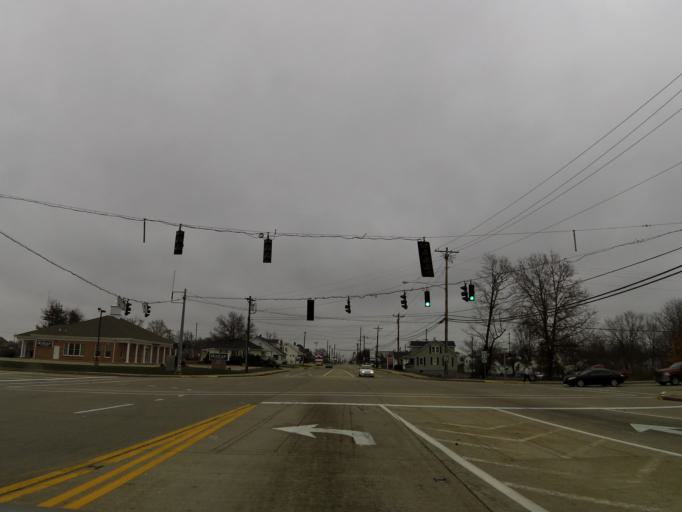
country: US
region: Kentucky
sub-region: Grant County
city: Dry Ridge
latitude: 38.6818
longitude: -84.5963
